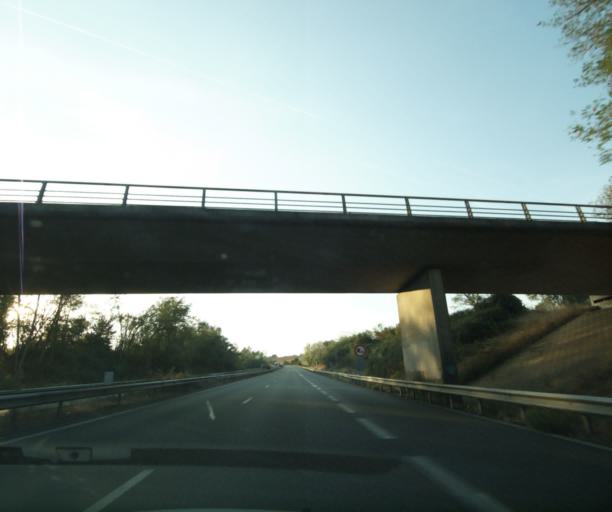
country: FR
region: Midi-Pyrenees
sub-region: Departement du Tarn-et-Garonne
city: Auvillar
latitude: 44.0647
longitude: 0.8572
